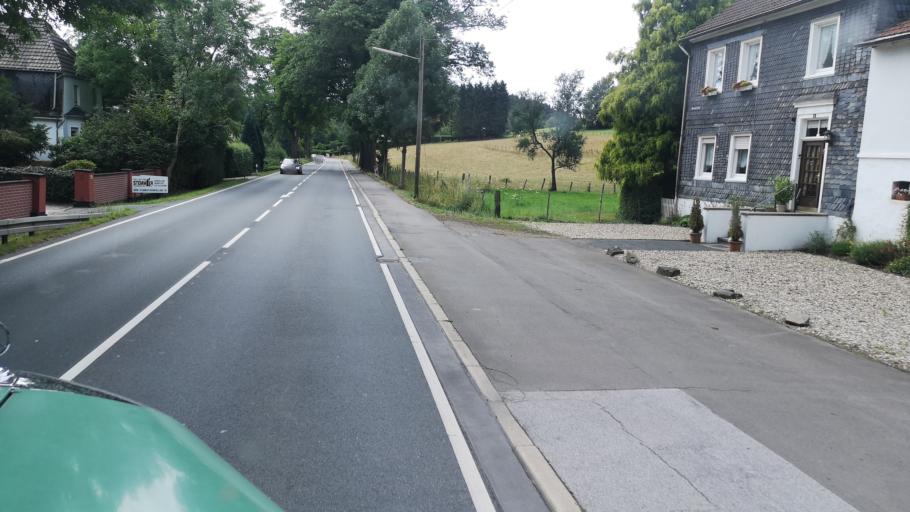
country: DE
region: North Rhine-Westphalia
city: Huckeswagen
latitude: 51.1363
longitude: 7.3459
